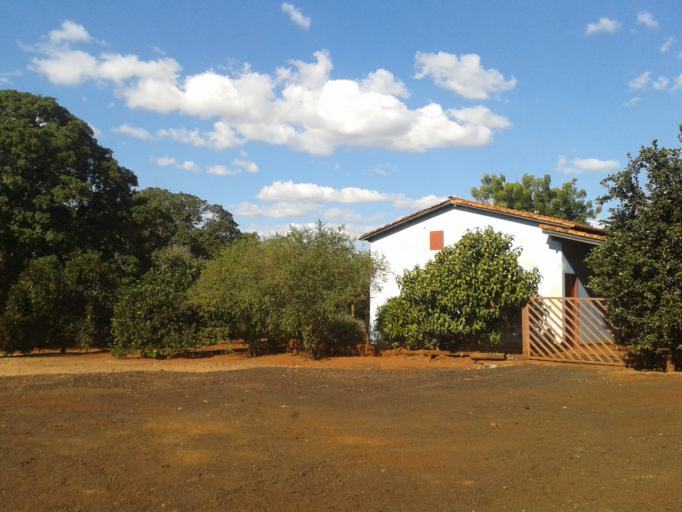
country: BR
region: Minas Gerais
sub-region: Centralina
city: Centralina
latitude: -18.5941
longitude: -49.2621
